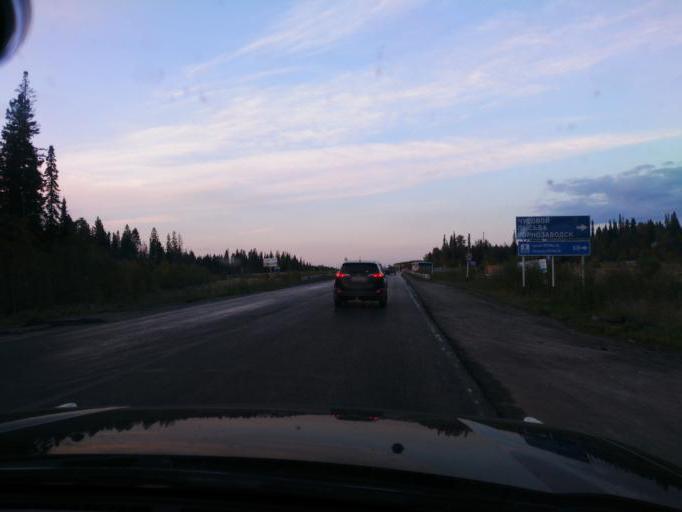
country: RU
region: Perm
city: Polazna
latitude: 58.2926
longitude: 56.4800
